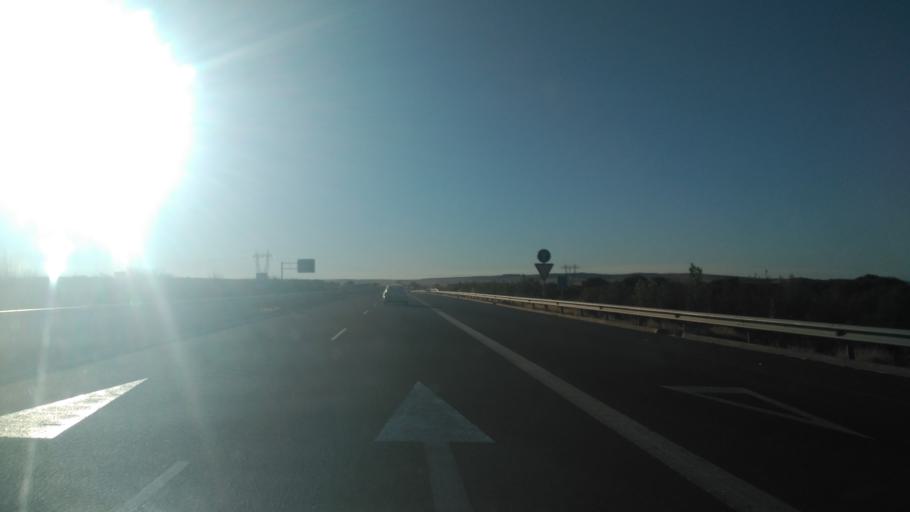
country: ES
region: Castille and Leon
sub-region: Provincia de Salamanca
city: Mozarbez
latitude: 40.8700
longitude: -5.6567
